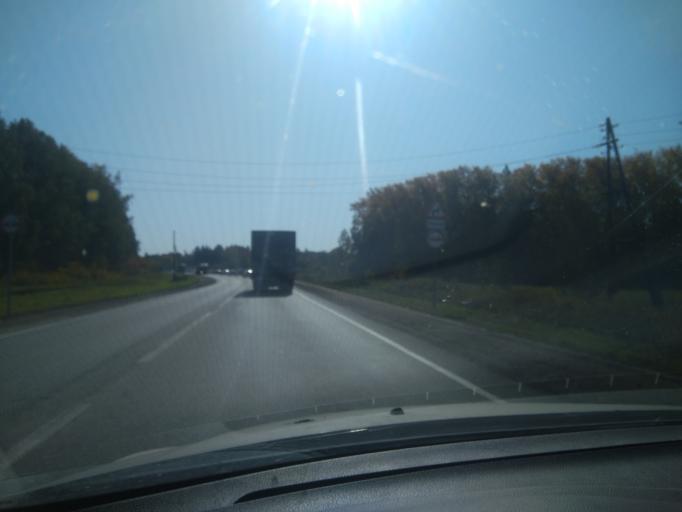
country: RU
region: Sverdlovsk
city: Sovkhoznyy
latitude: 56.6055
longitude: 61.3016
